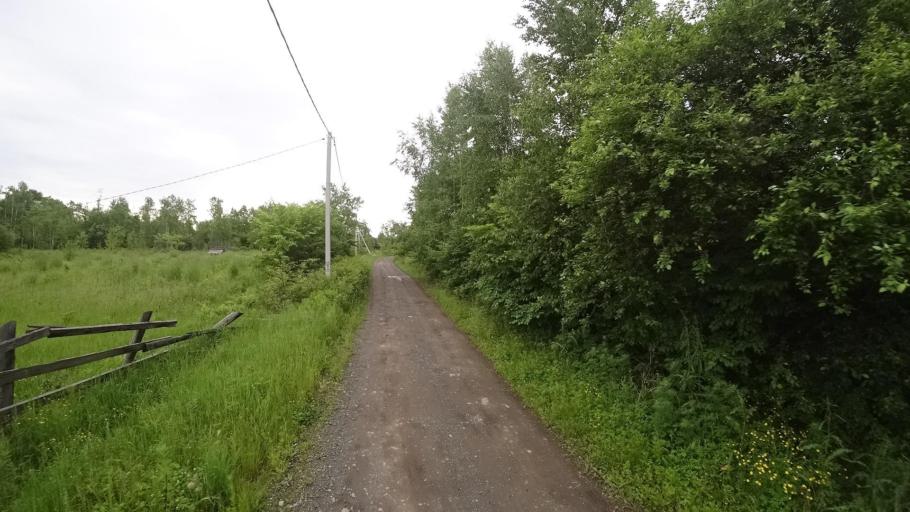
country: RU
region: Khabarovsk Krai
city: Amursk
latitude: 49.9038
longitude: 136.1357
